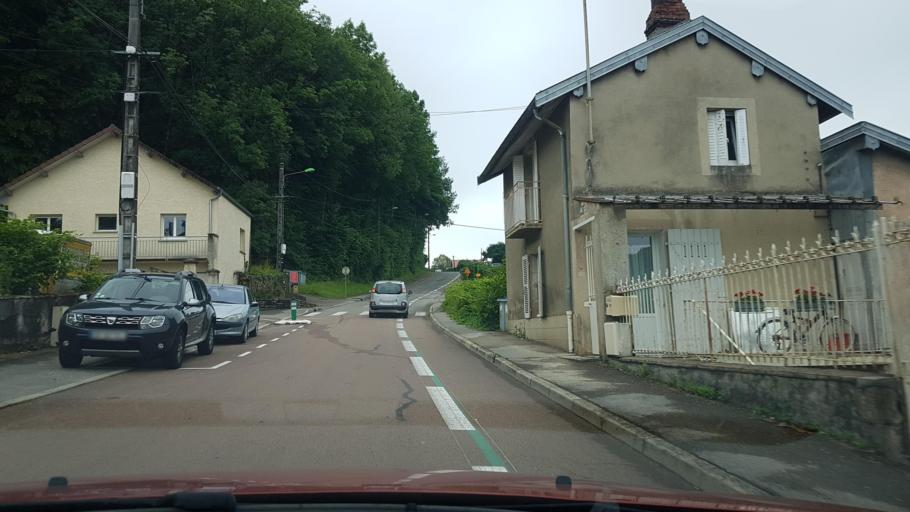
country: FR
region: Franche-Comte
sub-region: Departement du Jura
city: Lons-le-Saunier
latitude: 46.6714
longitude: 5.5373
